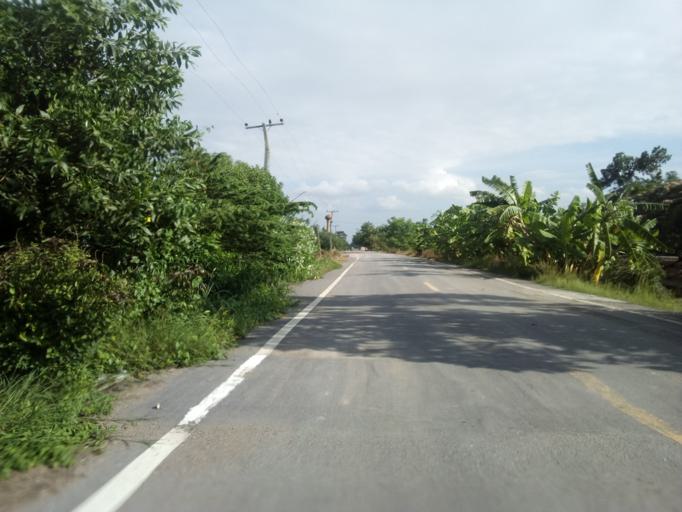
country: TH
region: Pathum Thani
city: Nong Suea
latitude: 14.2220
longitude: 100.8462
